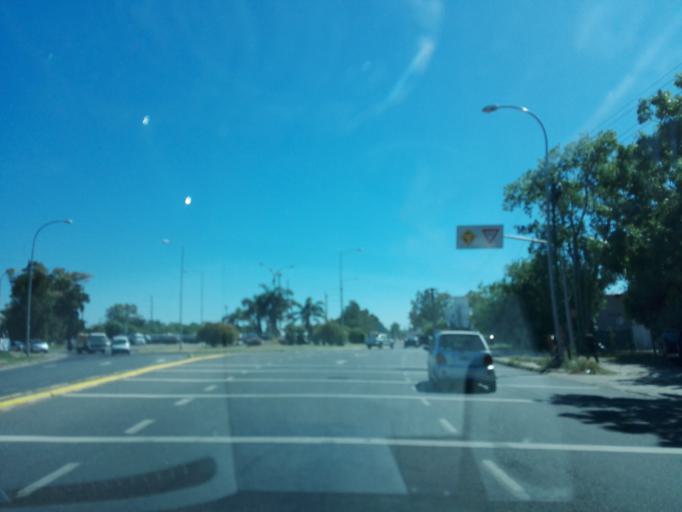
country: AR
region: Buenos Aires
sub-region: Partido de La Plata
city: La Plata
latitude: -34.9020
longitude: -57.9228
